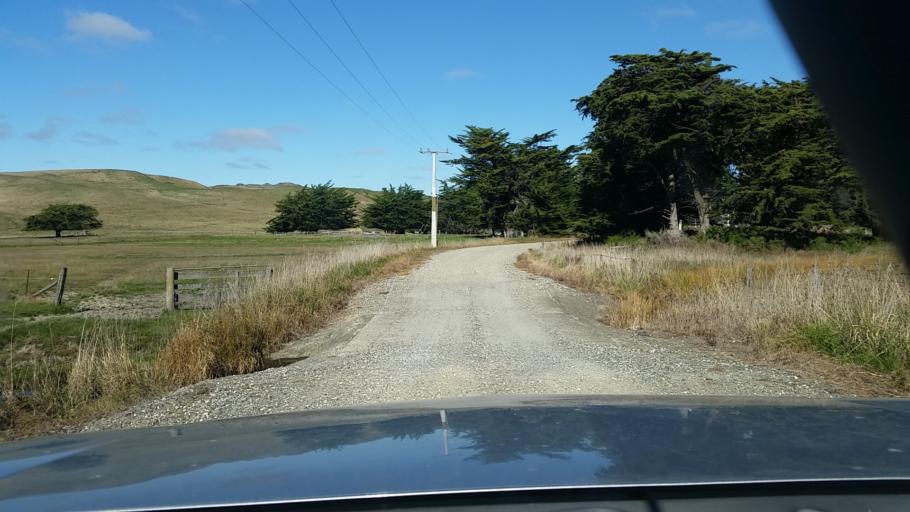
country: NZ
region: Marlborough
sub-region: Marlborough District
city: Blenheim
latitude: -41.7425
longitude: 174.1563
